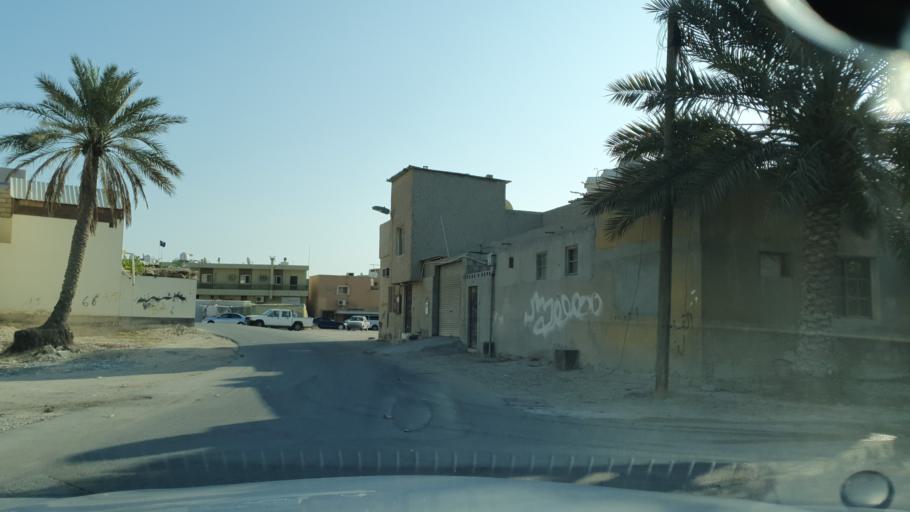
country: BH
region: Manama
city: Jidd Hafs
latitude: 26.2193
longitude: 50.4637
